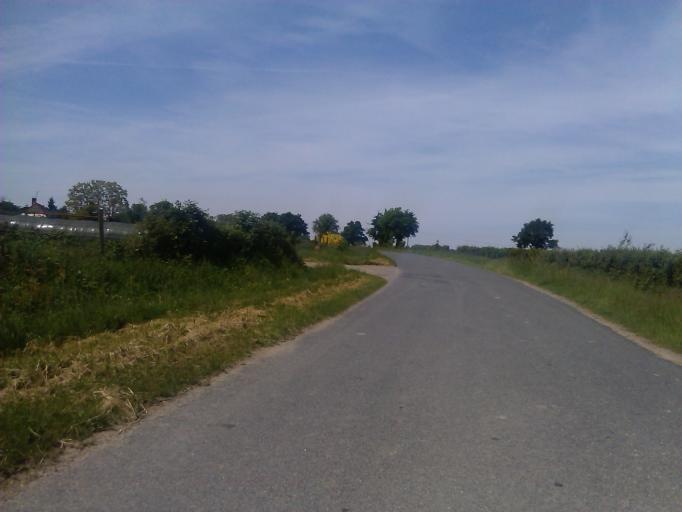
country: FR
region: Centre
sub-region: Departement du Cher
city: Orval
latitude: 46.5908
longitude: 2.4399
